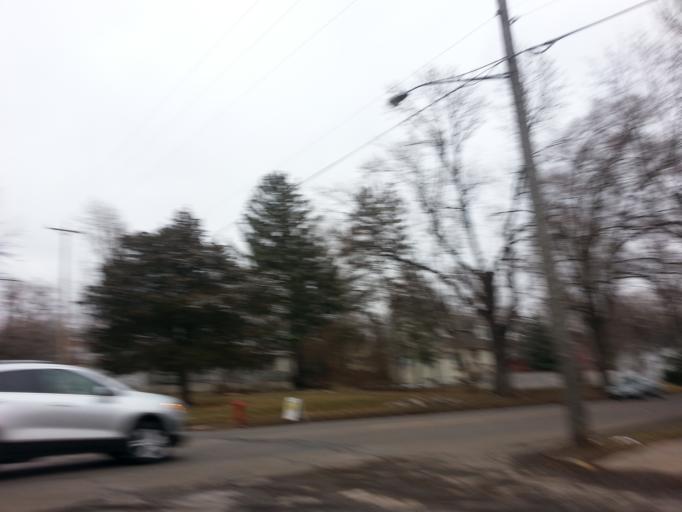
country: US
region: Wisconsin
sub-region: Saint Croix County
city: Hudson
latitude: 44.9839
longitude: -92.7574
